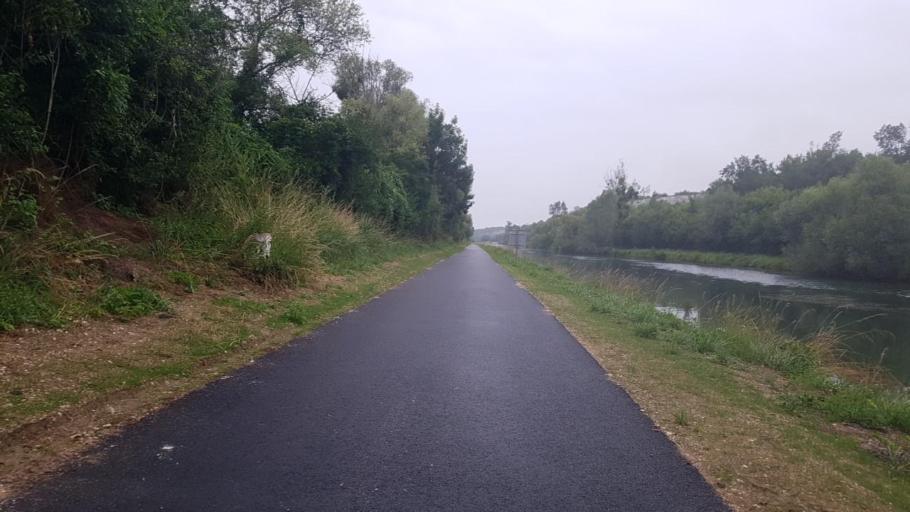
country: FR
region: Champagne-Ardenne
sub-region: Departement de la Marne
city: Vitry-le-Francois
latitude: 48.7808
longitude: 4.5393
